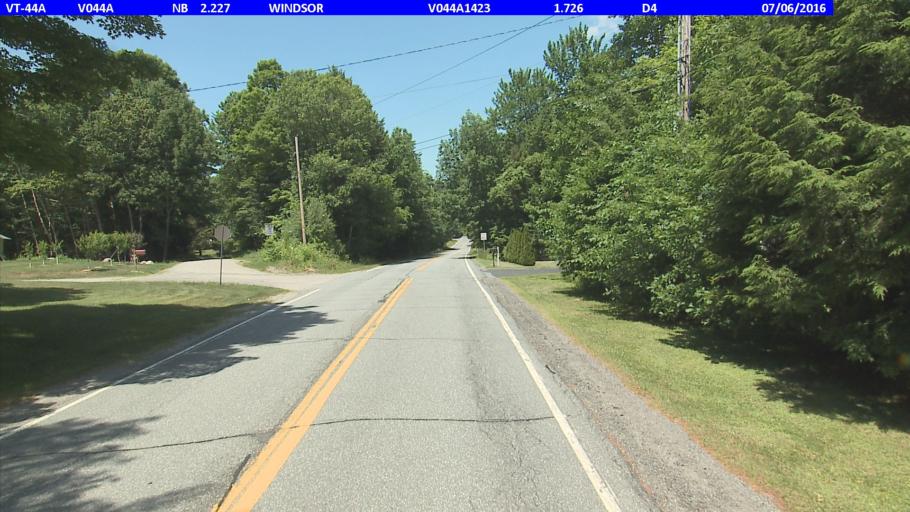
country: US
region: Vermont
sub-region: Windsor County
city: Windsor
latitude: 43.4502
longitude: -72.4163
